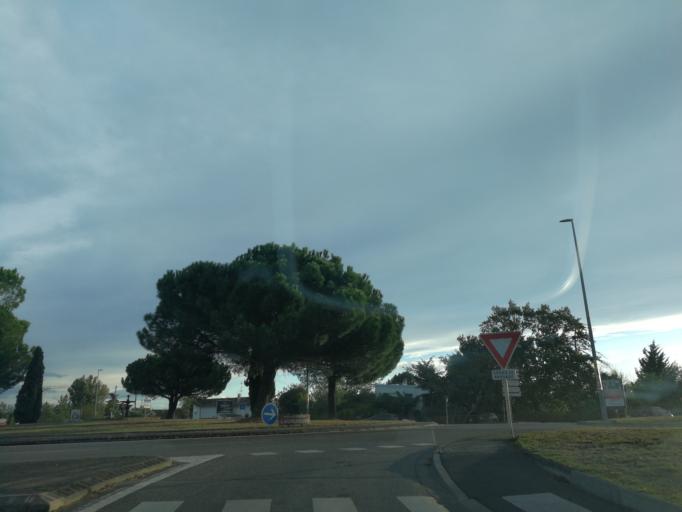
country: FR
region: Midi-Pyrenees
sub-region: Departement de la Haute-Garonne
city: Launaguet
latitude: 43.6599
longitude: 1.4548
